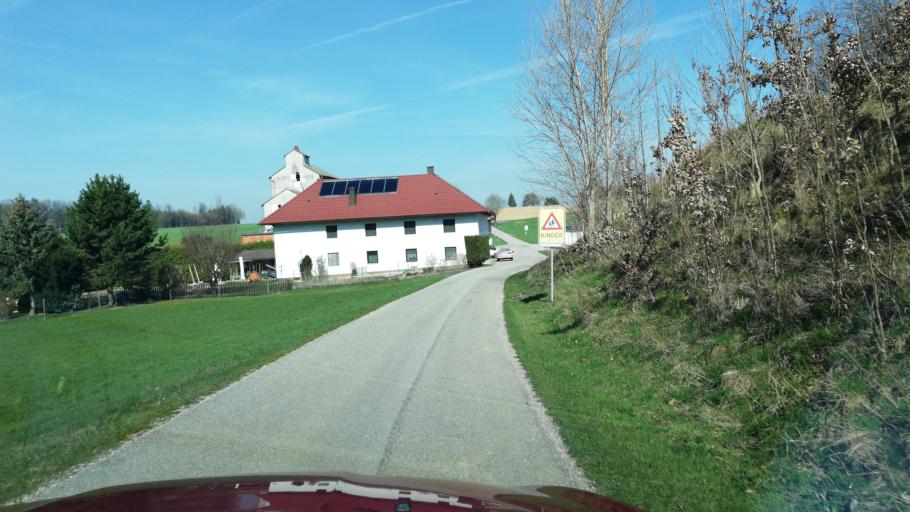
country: AT
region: Upper Austria
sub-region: Wels-Land
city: Sattledt
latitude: 48.1030
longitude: 14.0782
